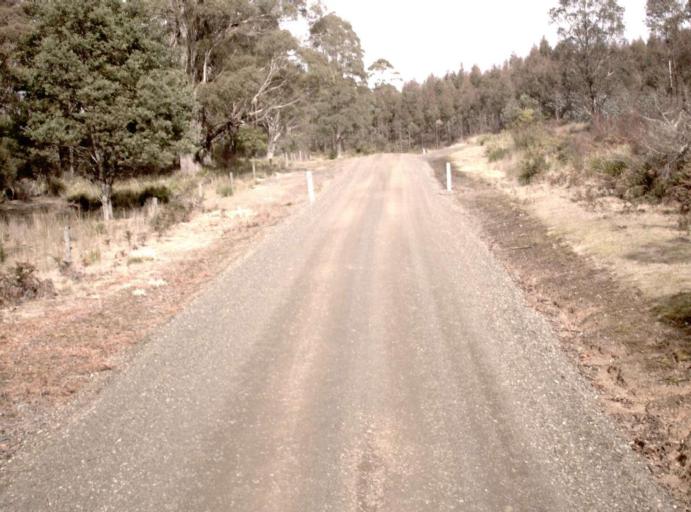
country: AU
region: Tasmania
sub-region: Northern Midlands
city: Evandale
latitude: -41.4522
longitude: 147.4770
